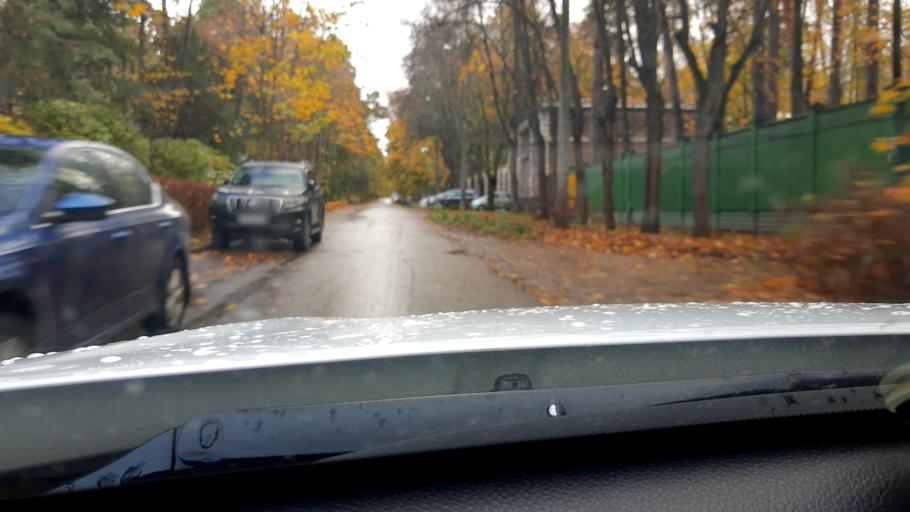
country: RU
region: Moscow
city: Shchukino
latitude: 55.7838
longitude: 37.4356
